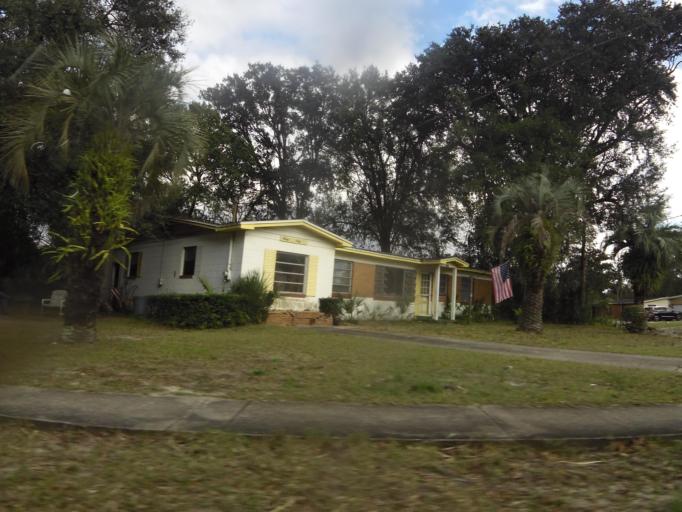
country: US
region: Florida
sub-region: Duval County
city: Jacksonville
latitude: 30.3604
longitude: -81.5897
